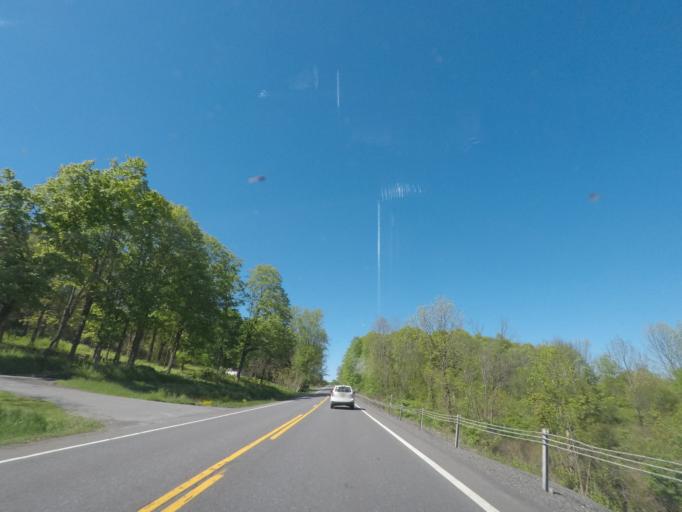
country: US
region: New York
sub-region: Greene County
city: Jefferson Heights
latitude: 42.2446
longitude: -73.8637
